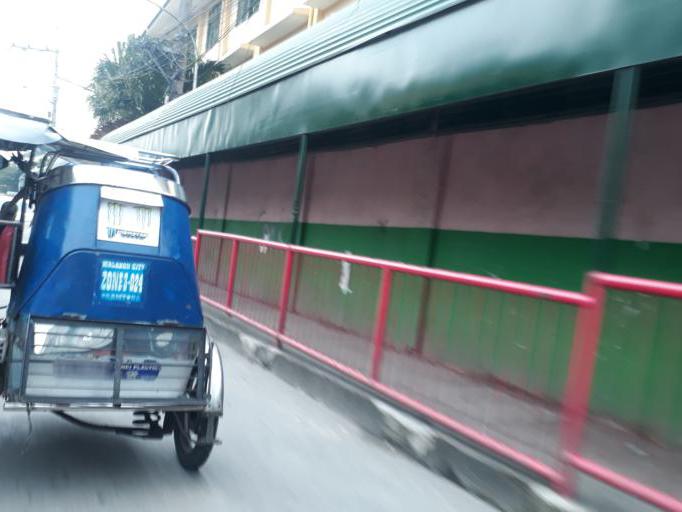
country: PH
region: Metro Manila
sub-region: Caloocan City
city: Niugan
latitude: 14.6607
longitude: 120.9676
